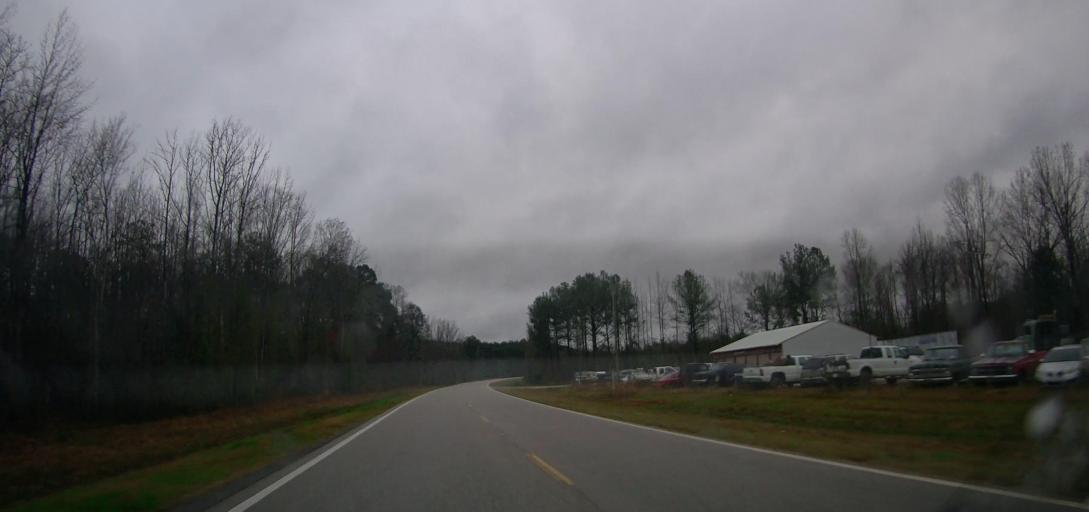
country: US
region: Alabama
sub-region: Bibb County
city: Centreville
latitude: 32.9206
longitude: -87.0334
